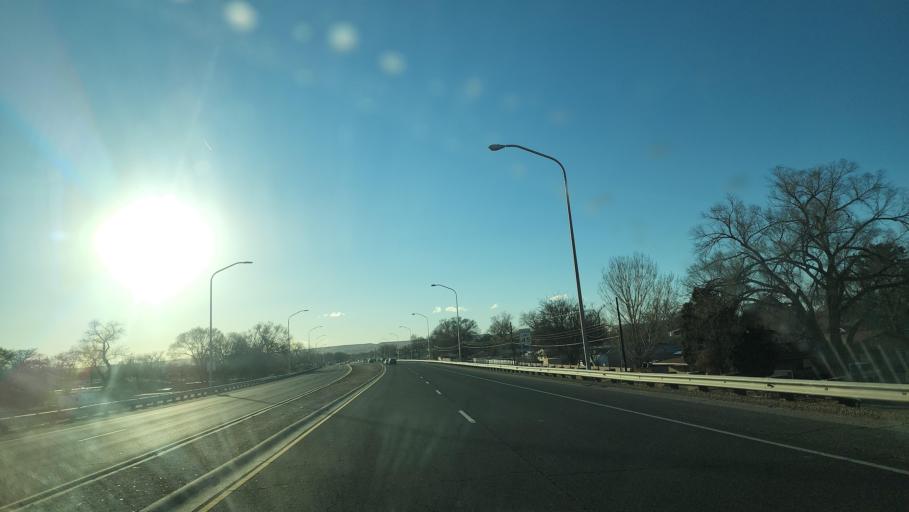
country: US
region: New Mexico
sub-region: Bernalillo County
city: South Valley
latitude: 35.0272
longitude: -106.6749
